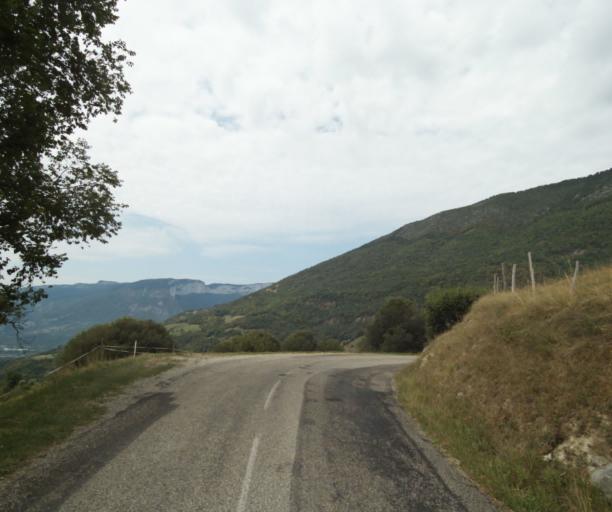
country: FR
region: Rhone-Alpes
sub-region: Departement de l'Isere
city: Saint-Egreve
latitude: 45.2592
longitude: 5.7085
